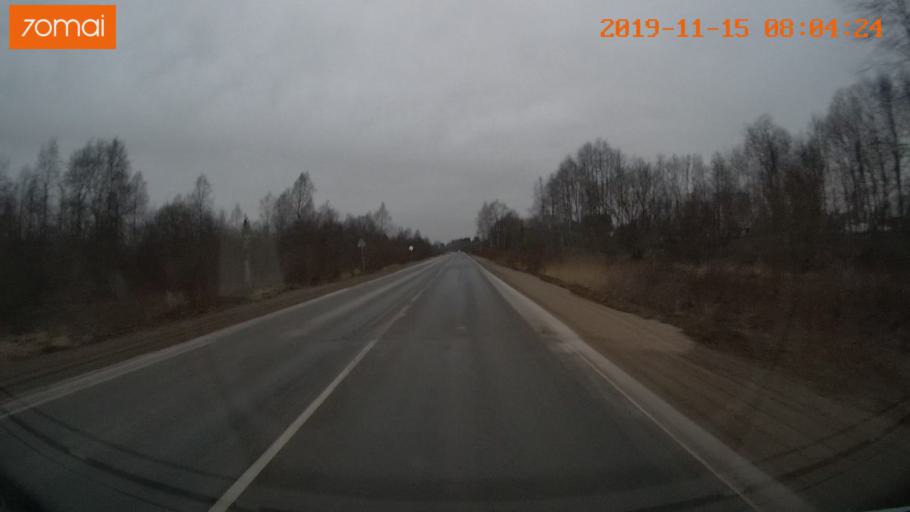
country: RU
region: Vologda
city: Cherepovets
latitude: 59.0080
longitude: 38.0765
